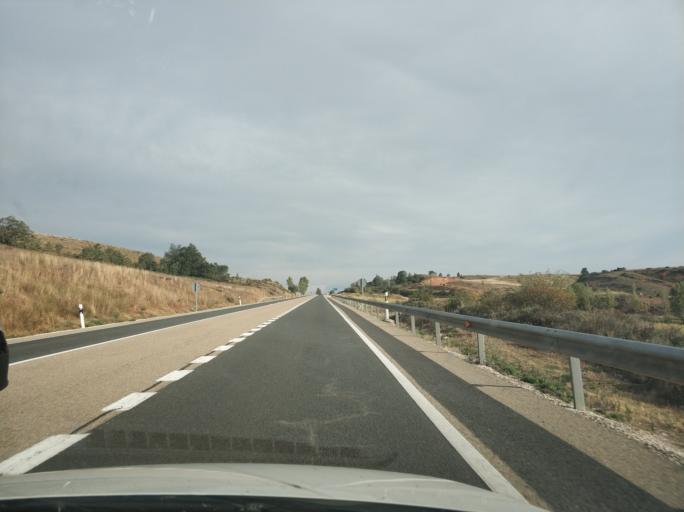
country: ES
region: Castille and Leon
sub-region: Provincia de Burgos
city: Huermeces
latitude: 42.5532
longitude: -3.7453
